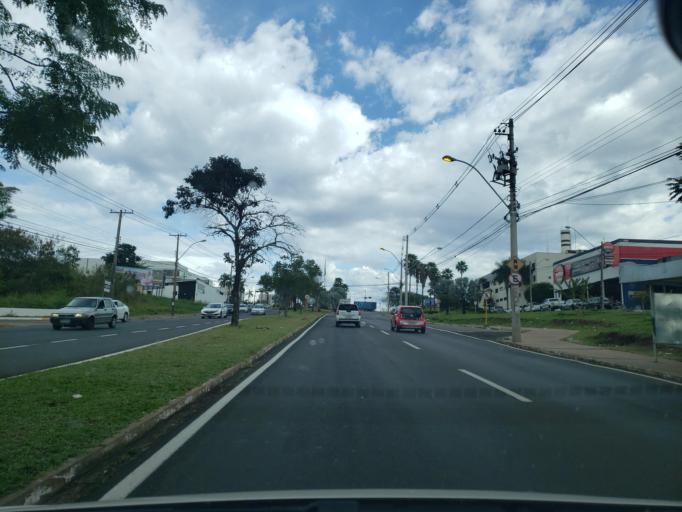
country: BR
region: Sao Paulo
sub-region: Bauru
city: Bauru
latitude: -22.3382
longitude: -49.0431
